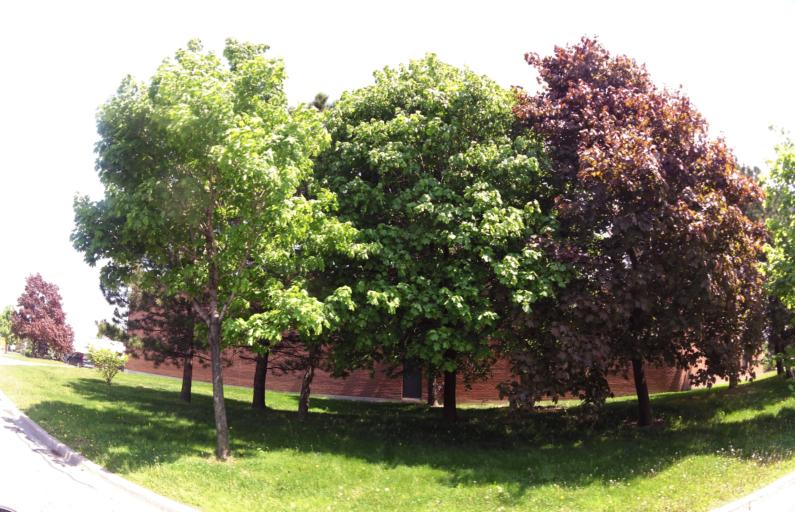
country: CA
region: Ontario
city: Mississauga
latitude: 43.6382
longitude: -79.6510
